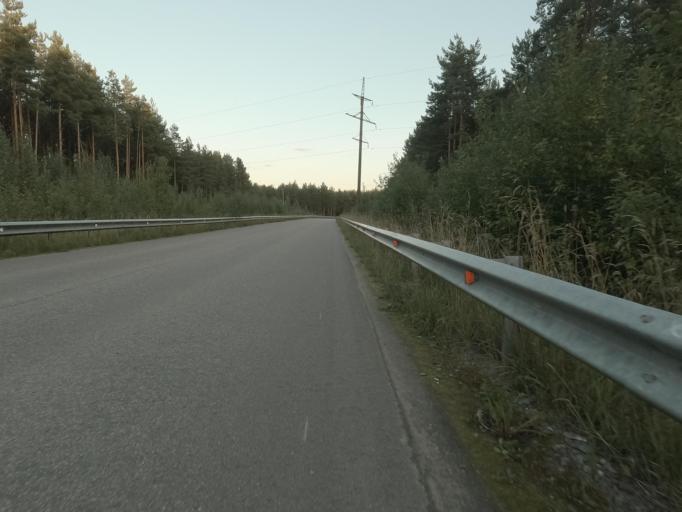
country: RU
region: Leningrad
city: Mga
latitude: 59.7629
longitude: 31.0387
